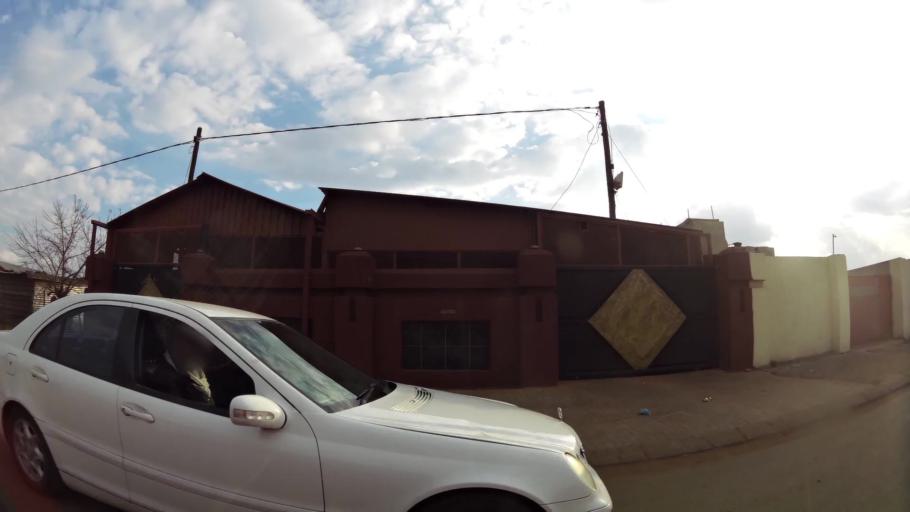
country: ZA
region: Gauteng
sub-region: Sedibeng District Municipality
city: Vanderbijlpark
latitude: -26.6771
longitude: 27.8689
